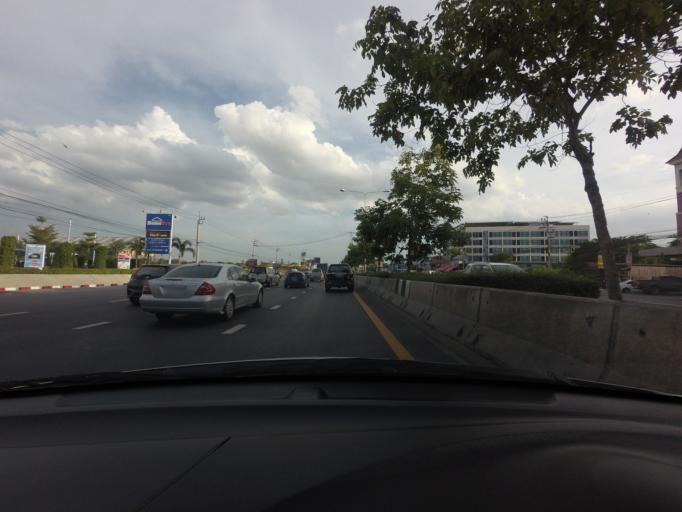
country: TH
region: Nonthaburi
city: Bang Bua Thong
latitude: 13.9174
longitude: 100.4515
